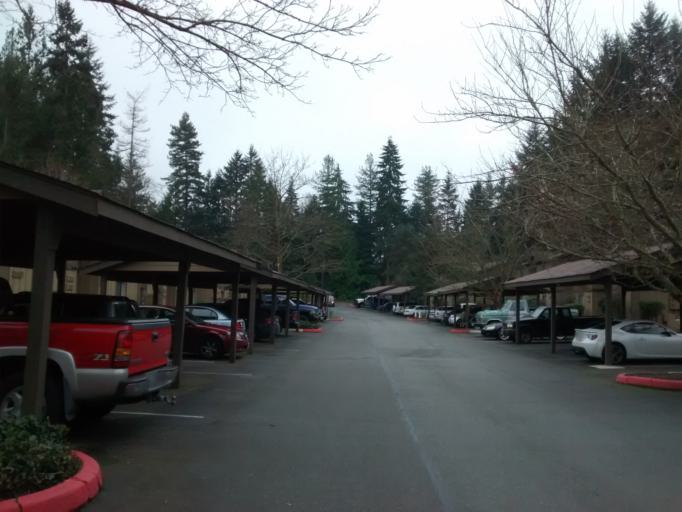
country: US
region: Washington
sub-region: Kitsap County
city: Parkwood
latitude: 47.5208
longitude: -122.6057
